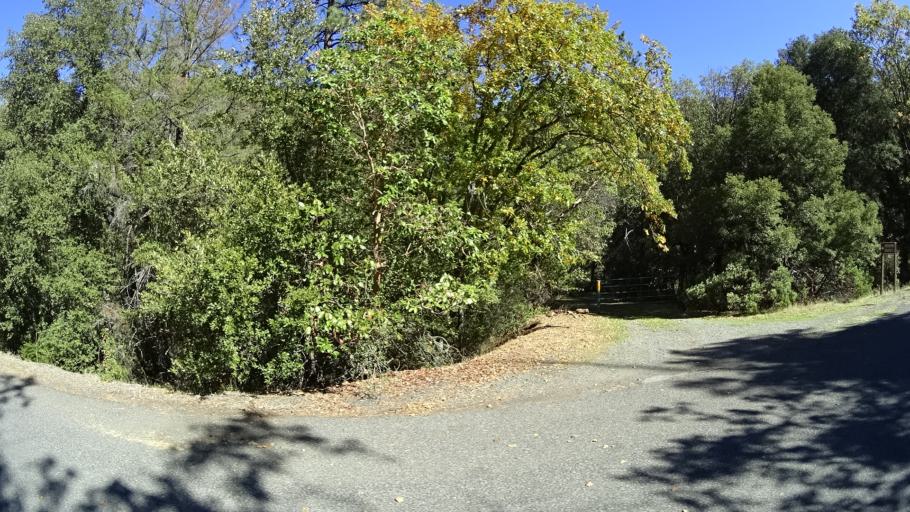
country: US
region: California
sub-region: Humboldt County
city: Willow Creek
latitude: 41.2963
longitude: -123.3625
